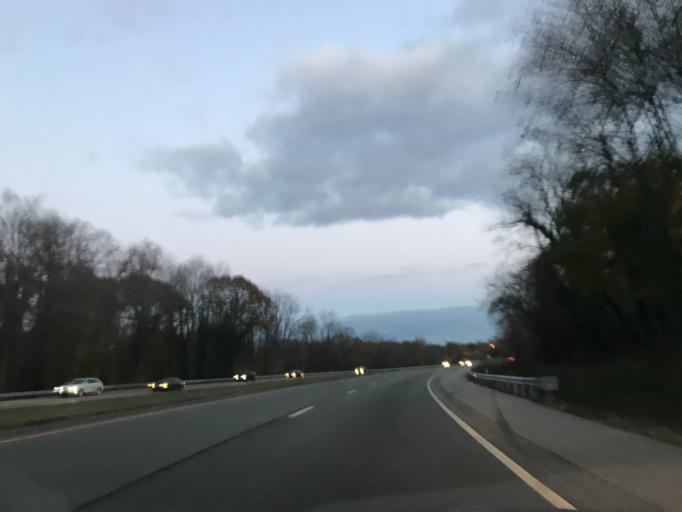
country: US
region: Delaware
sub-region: New Castle County
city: Claymont
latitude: 39.8044
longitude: -75.4758
